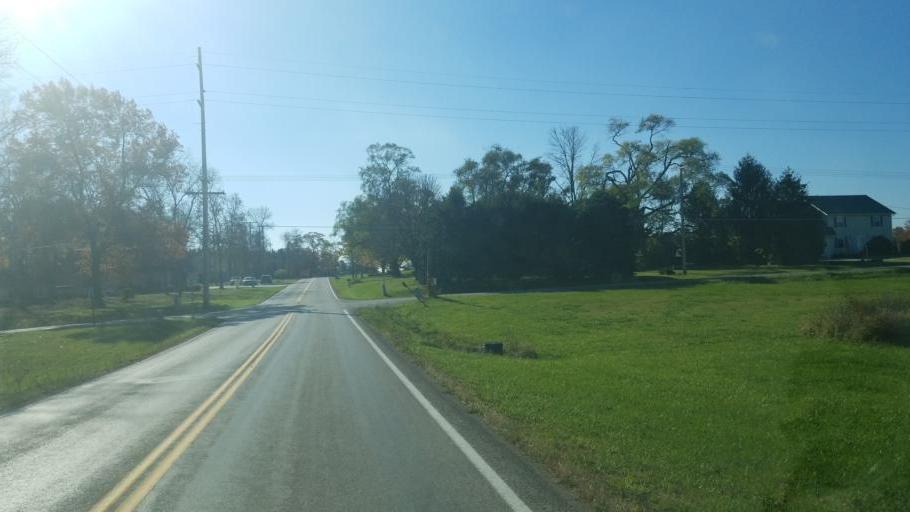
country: US
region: Ohio
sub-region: Ashland County
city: Ashland
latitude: 40.8295
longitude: -82.3337
